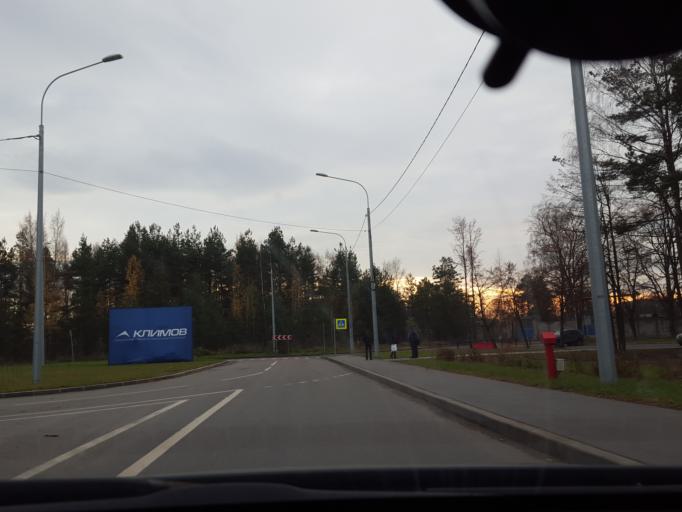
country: RU
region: St.-Petersburg
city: Kolomyagi
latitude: 60.0468
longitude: 30.2458
